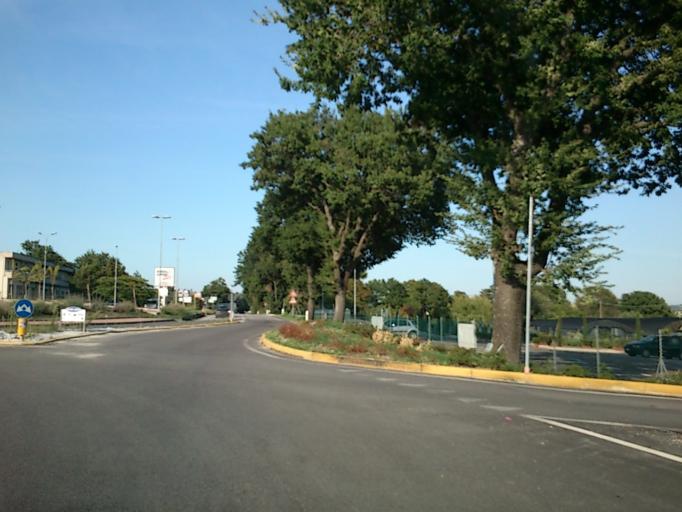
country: IT
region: The Marches
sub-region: Provincia di Pesaro e Urbino
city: Fossombrone
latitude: 43.7022
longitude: 12.8332
